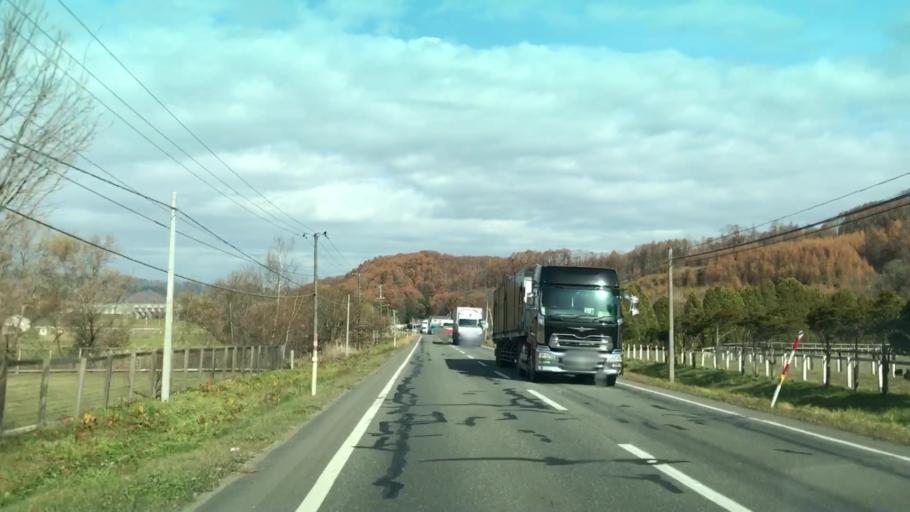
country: JP
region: Hokkaido
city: Shizunai-furukawacho
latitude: 42.6137
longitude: 142.1486
